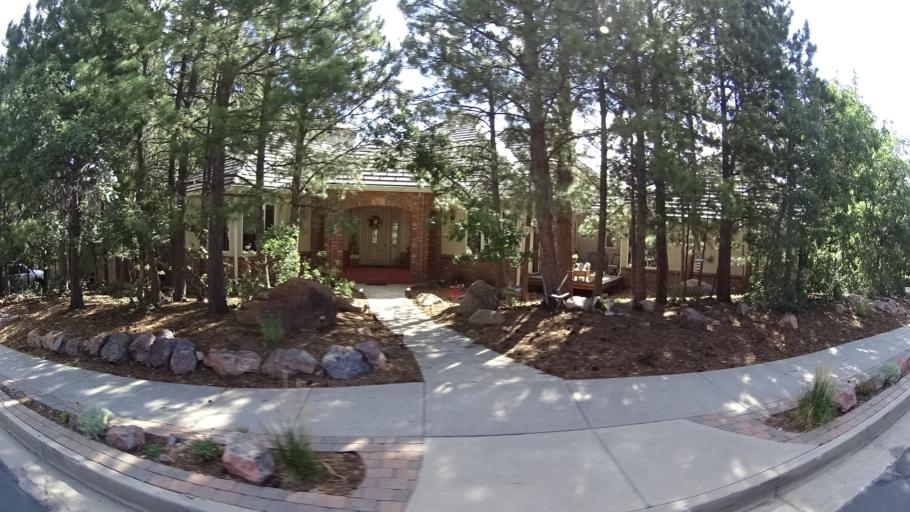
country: US
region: Colorado
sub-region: El Paso County
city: Fort Carson
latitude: 38.7611
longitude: -104.8362
